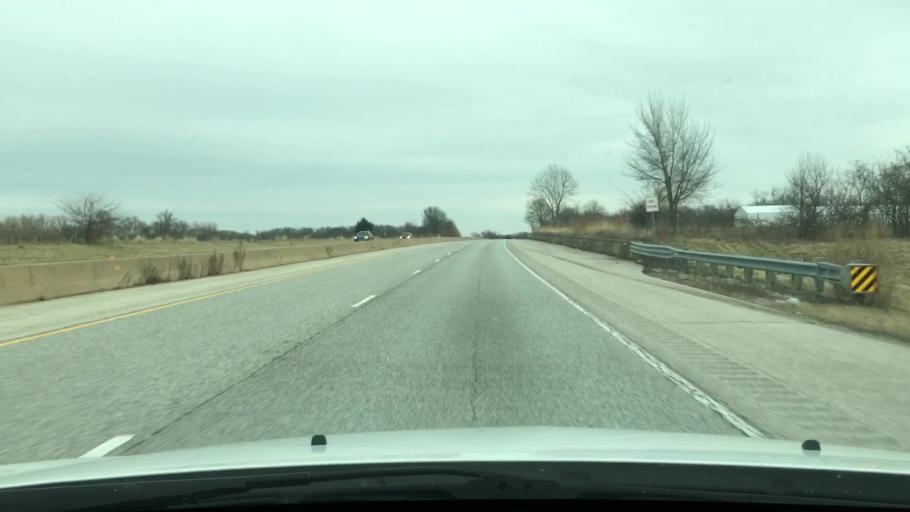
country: US
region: Illinois
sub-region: Pike County
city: Griggsville
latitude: 39.6811
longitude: -90.6712
